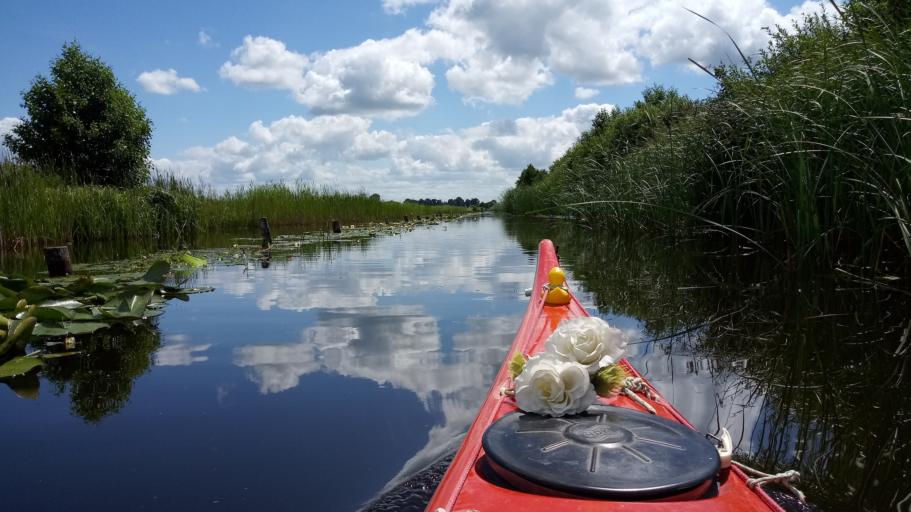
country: NL
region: Overijssel
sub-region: Gemeente Steenwijkerland
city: Wanneperveen
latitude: 52.7054
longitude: 6.0913
